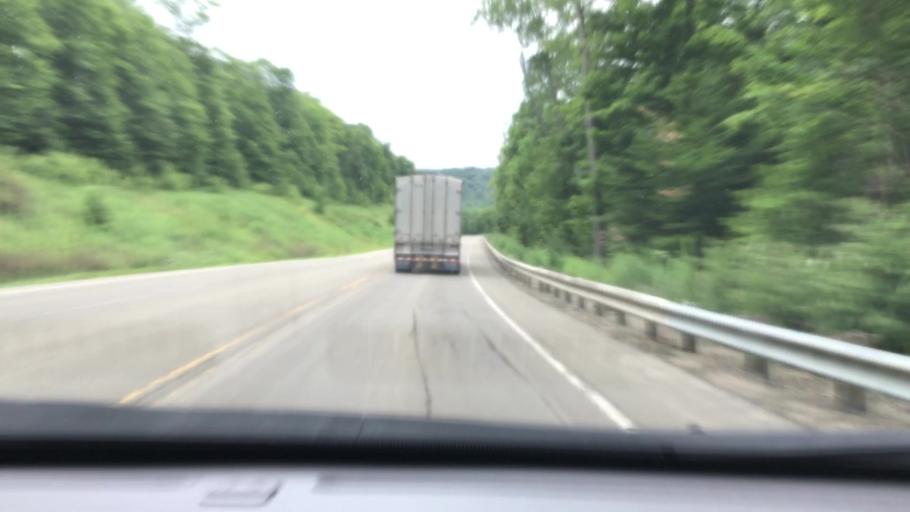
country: US
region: Pennsylvania
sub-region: McKean County
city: Kane
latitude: 41.7546
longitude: -78.6959
